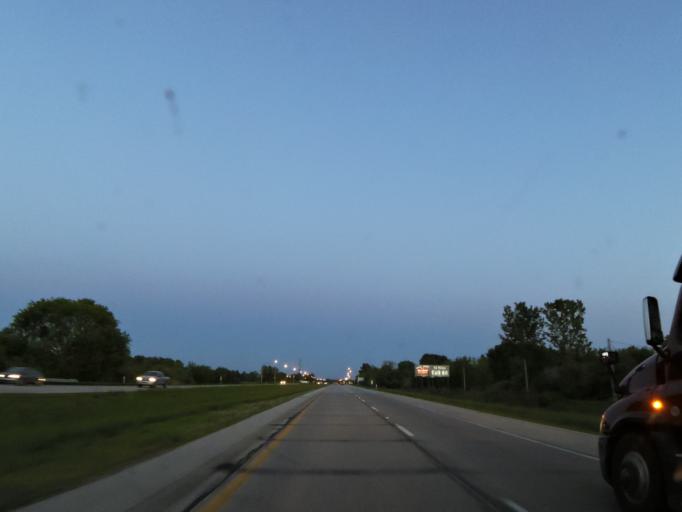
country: US
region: Indiana
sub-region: Hendricks County
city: Pittsboro
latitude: 39.9069
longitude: -86.5623
